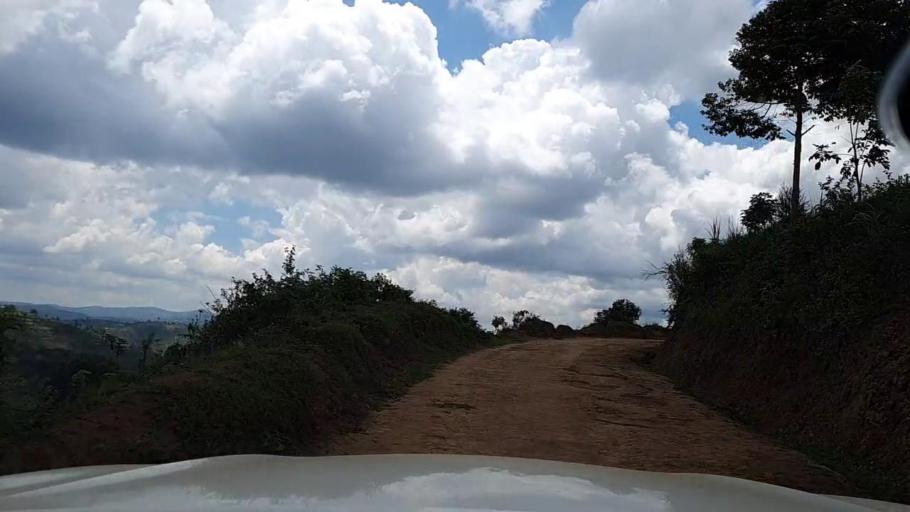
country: RW
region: Southern Province
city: Nzega
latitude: -2.6370
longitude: 29.4881
